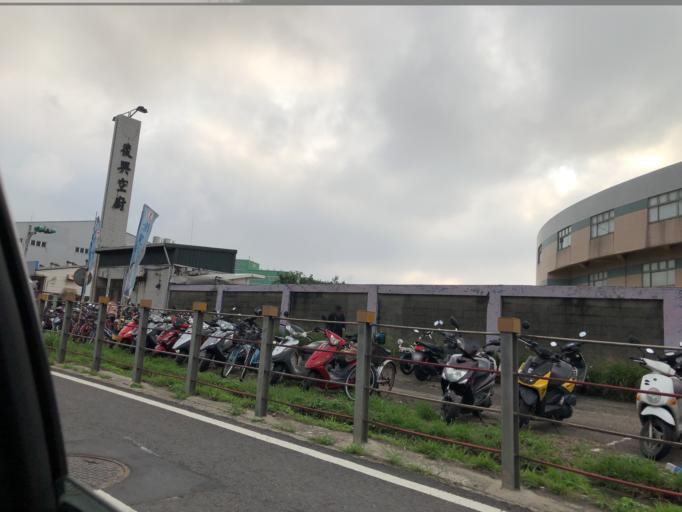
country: TW
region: Taiwan
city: Taoyuan City
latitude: 25.0959
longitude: 121.2497
